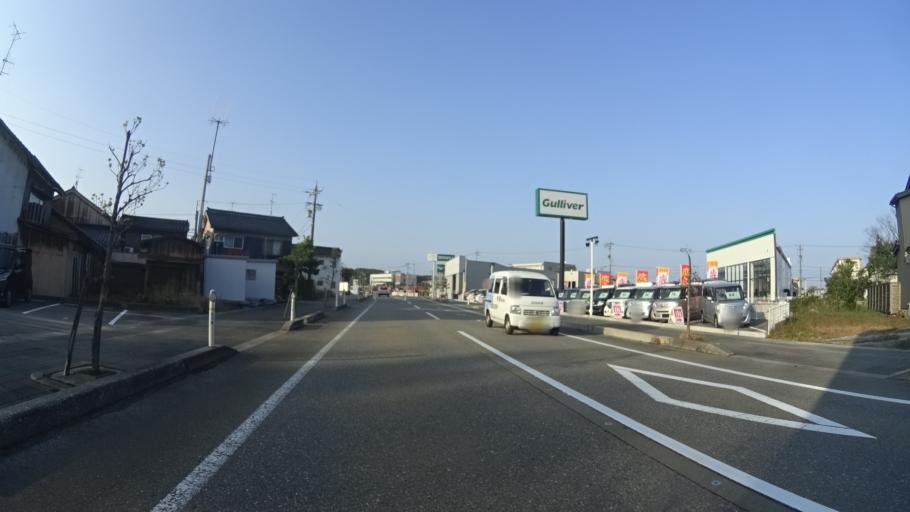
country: JP
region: Ishikawa
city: Nanao
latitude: 37.0515
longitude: 136.9561
